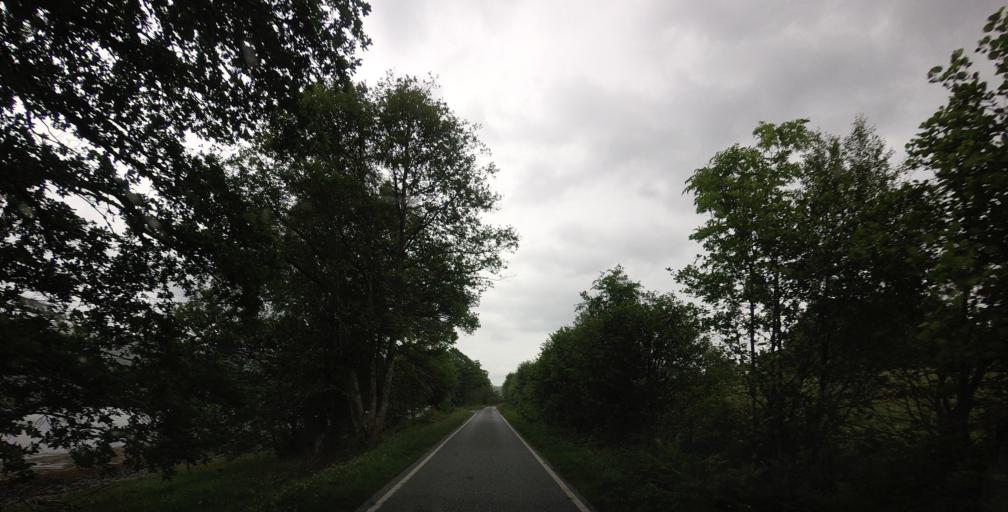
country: GB
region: Scotland
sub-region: Highland
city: Fort William
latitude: 56.8447
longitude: -5.2103
